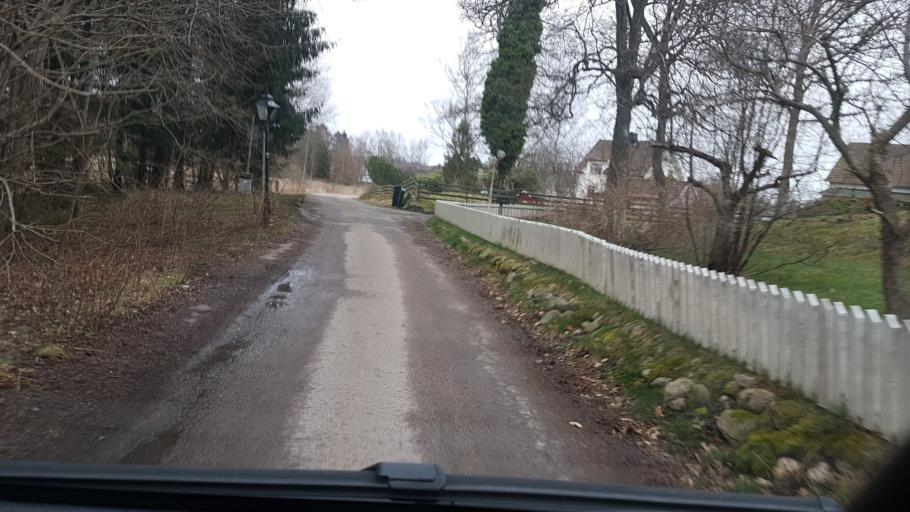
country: SE
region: Vaestra Goetaland
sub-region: Lerums Kommun
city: Stenkullen
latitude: 57.7918
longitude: 12.3049
